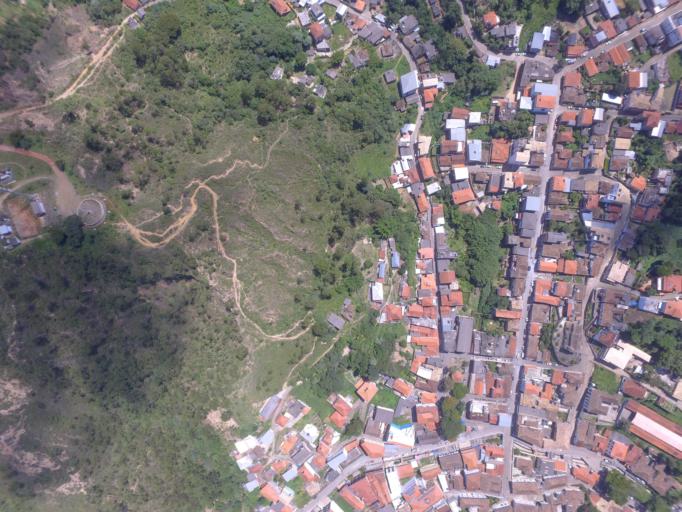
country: BR
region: Minas Gerais
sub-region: Tiradentes
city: Tiradentes
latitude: -21.0558
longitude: -44.0780
